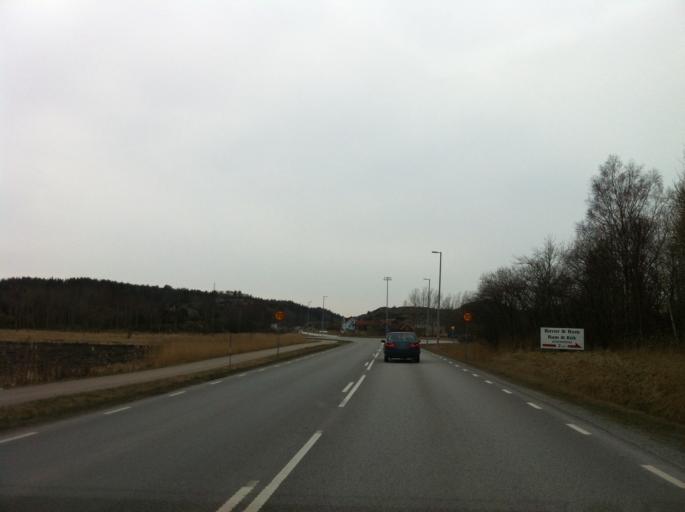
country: SE
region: Vaestra Goetaland
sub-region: Orust
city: Henan
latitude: 58.1886
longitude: 11.6914
